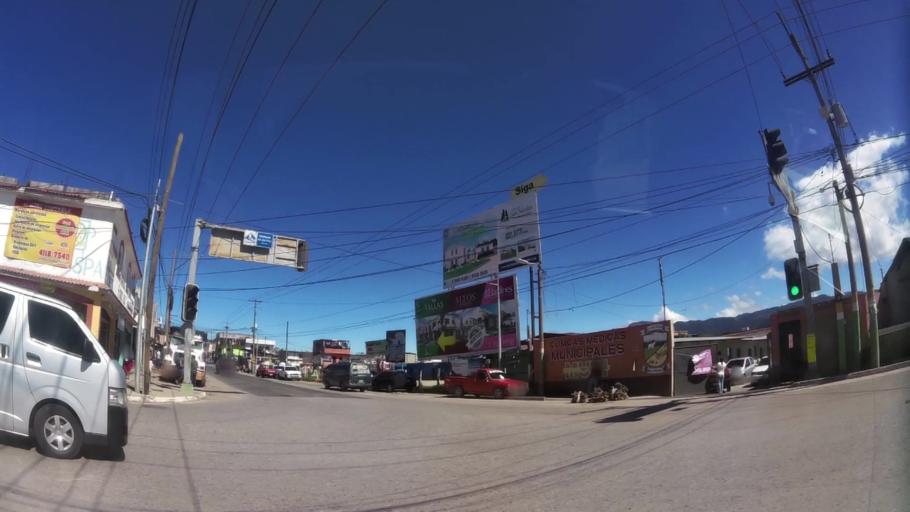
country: GT
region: Guatemala
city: San Jose Pinula
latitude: 14.5458
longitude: -90.4089
